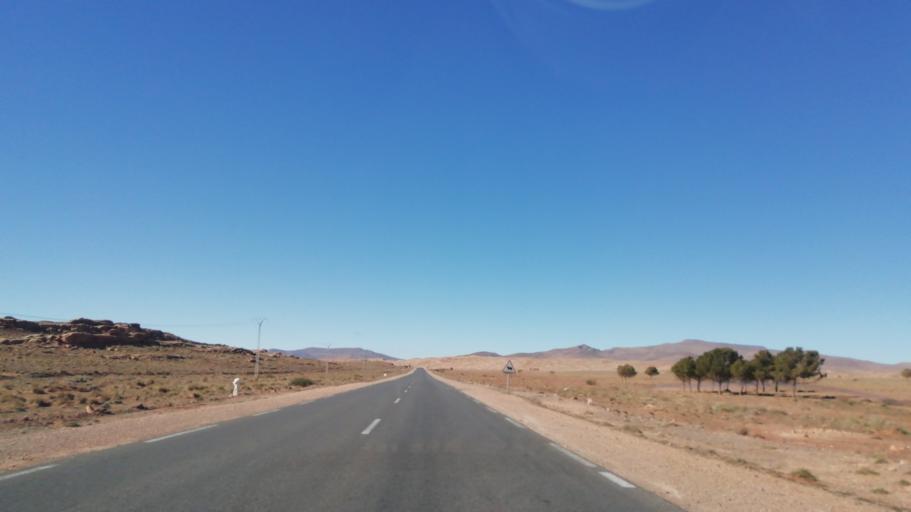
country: DZ
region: El Bayadh
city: El Bayadh
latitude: 33.6160
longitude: 1.2096
